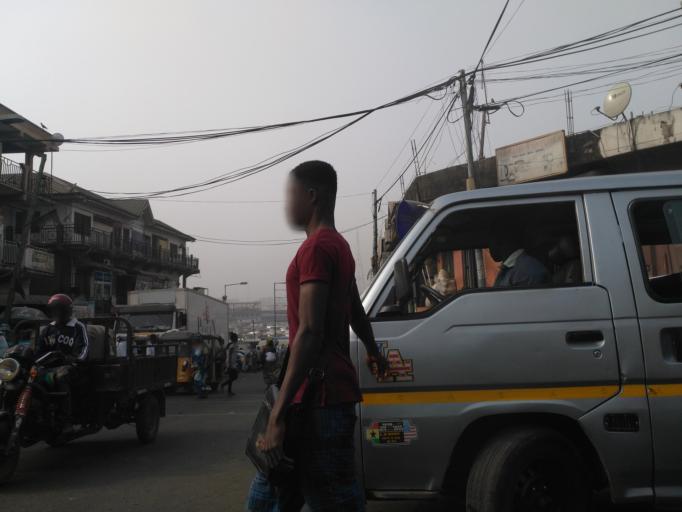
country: GH
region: Ashanti
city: Kumasi
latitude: 6.7001
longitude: -1.6181
